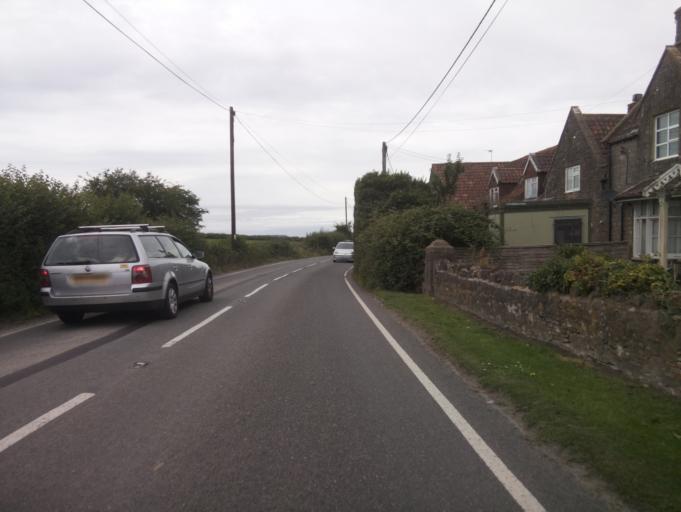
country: GB
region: England
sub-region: North Somerset
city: Congresbury
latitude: 51.3560
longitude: -2.7989
